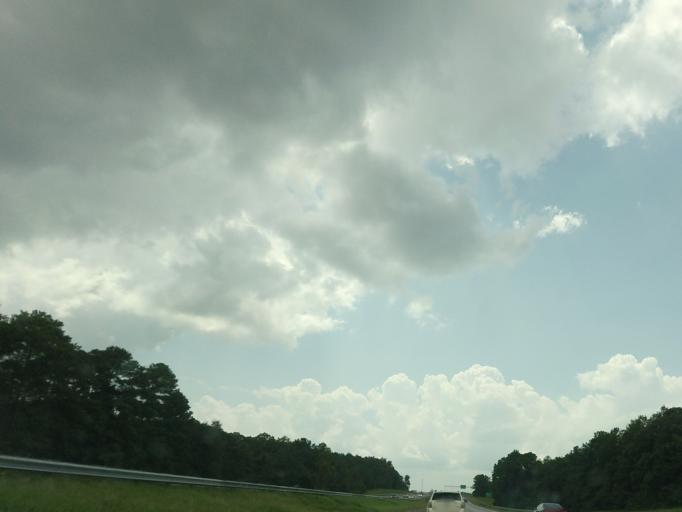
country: US
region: Georgia
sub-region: Houston County
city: Centerville
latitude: 32.5567
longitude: -83.7443
